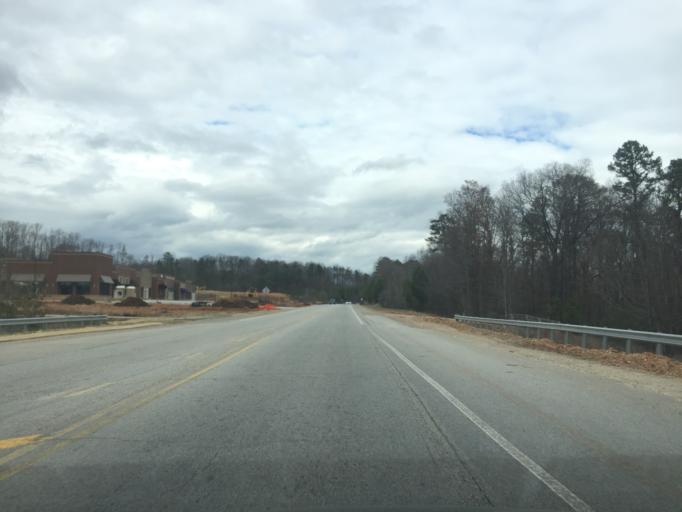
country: US
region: Tennessee
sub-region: Hamilton County
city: Collegedale
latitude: 35.0678
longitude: -85.0726
